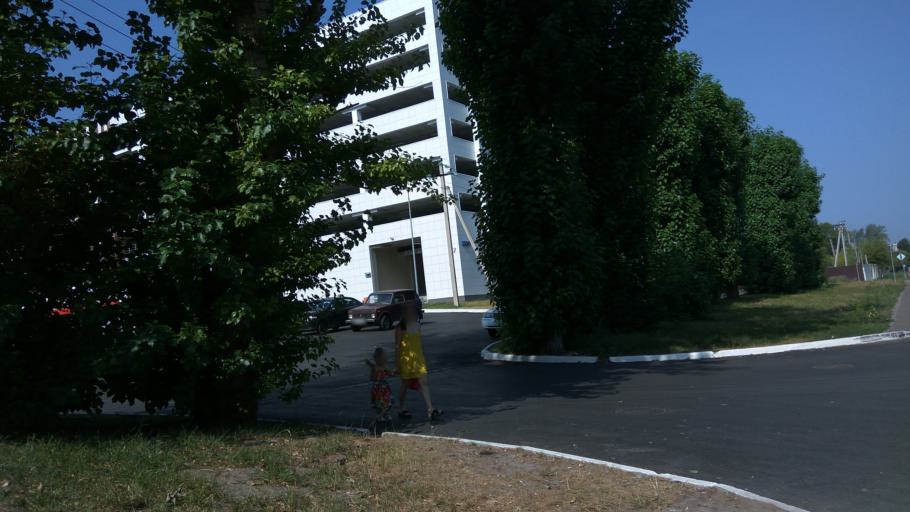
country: RU
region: Tatarstan
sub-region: Gorod Kazan'
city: Kazan
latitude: 55.7692
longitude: 49.1520
